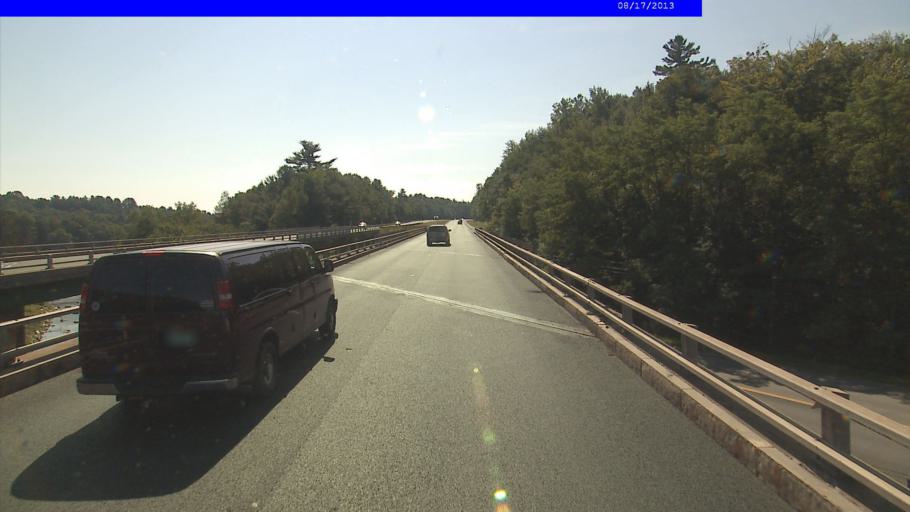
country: US
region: Vermont
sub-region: Windham County
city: Bellows Falls
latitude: 43.1236
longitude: -72.4685
